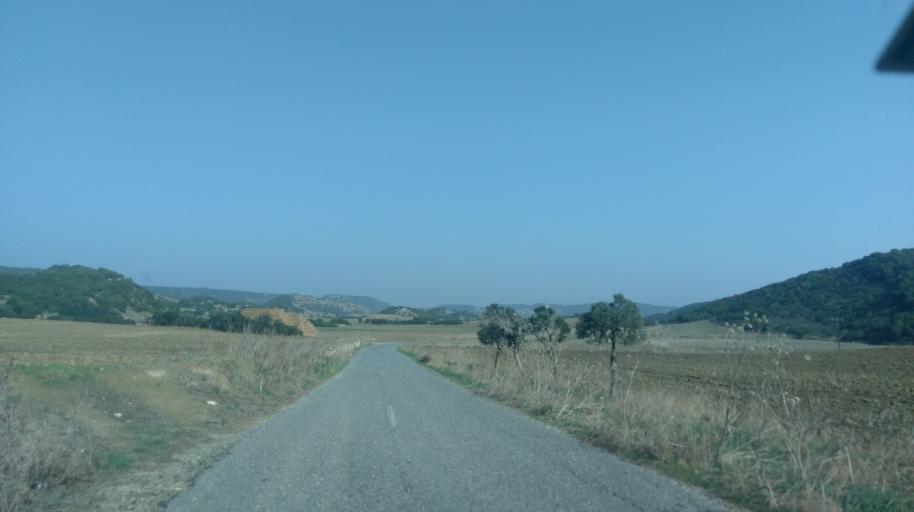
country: CY
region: Ammochostos
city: Rizokarpaso
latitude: 35.6372
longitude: 34.5113
